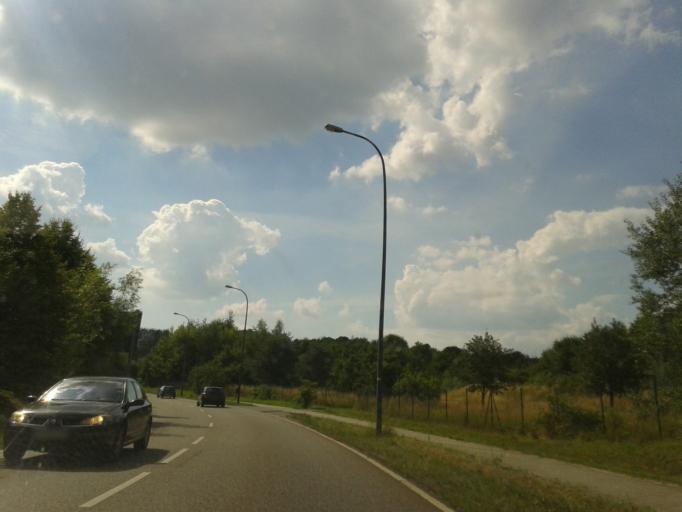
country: DE
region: Saxony
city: Bannewitz
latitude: 51.0147
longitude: 13.7195
